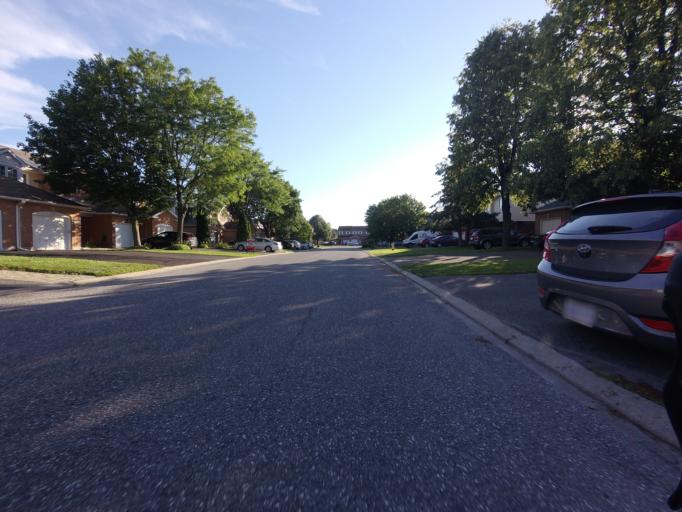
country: CA
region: Ontario
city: Bells Corners
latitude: 45.2899
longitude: -75.7323
